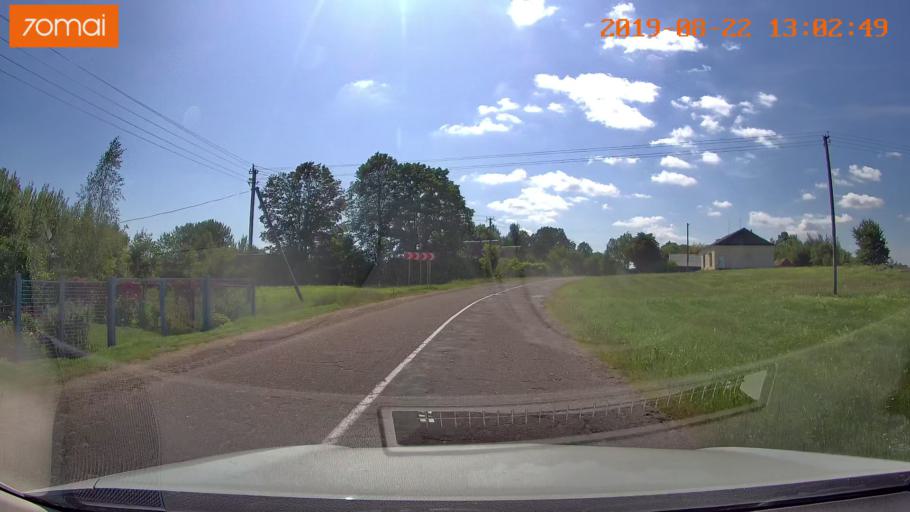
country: BY
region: Minsk
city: Prawdzinski
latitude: 53.3852
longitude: 27.8250
